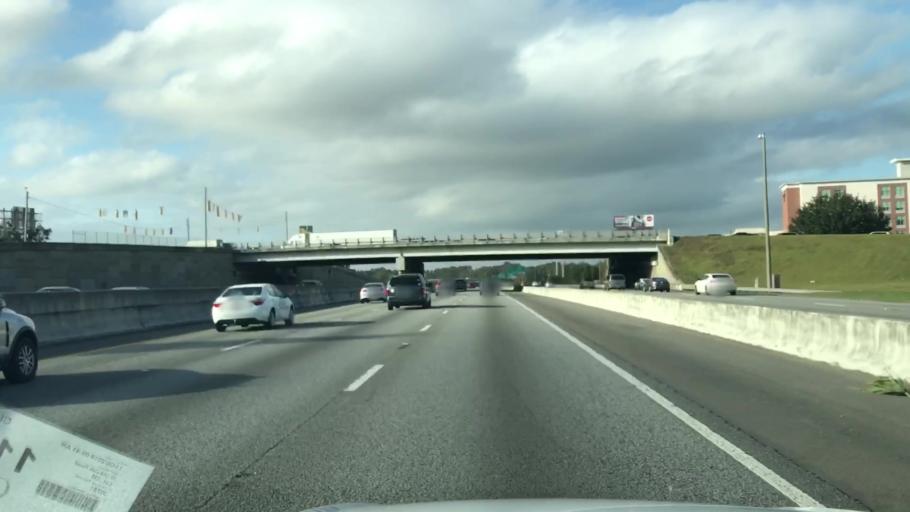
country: US
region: South Carolina
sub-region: Berkeley County
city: Hanahan
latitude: 32.9337
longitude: -80.0468
